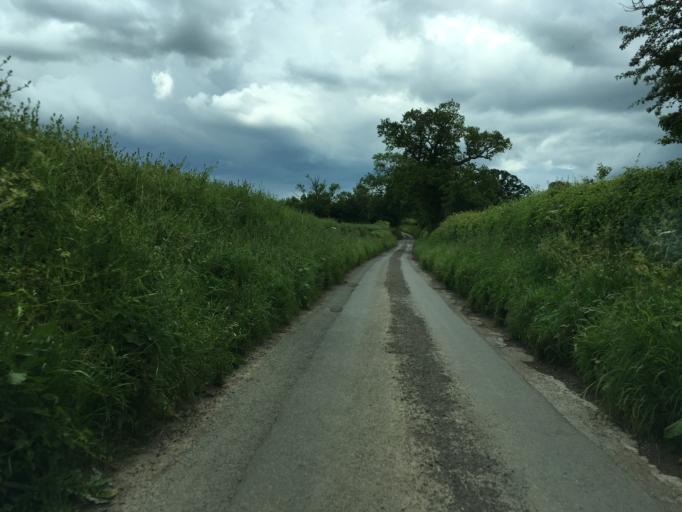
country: GB
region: England
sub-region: Wiltshire
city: Hankerton
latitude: 51.6463
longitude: -2.0147
